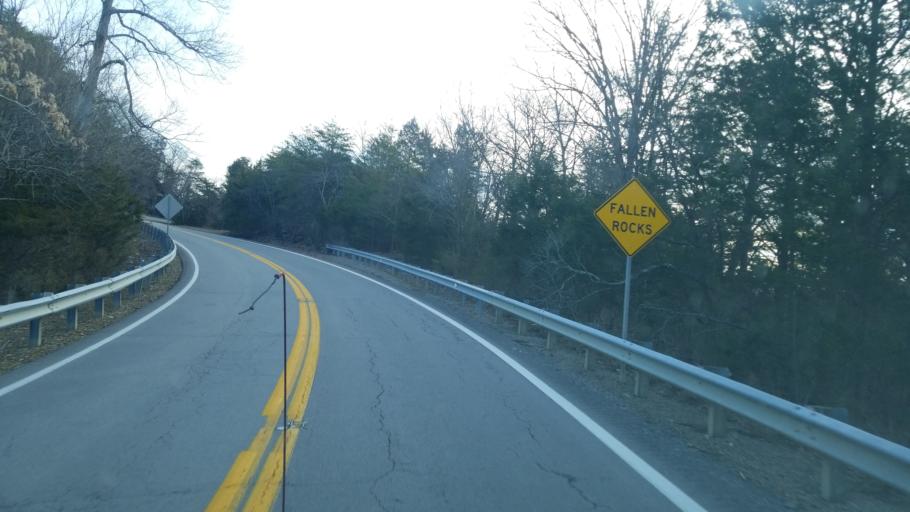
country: US
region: Kentucky
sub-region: Russell County
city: Jamestown
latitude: 36.8706
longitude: -85.1258
